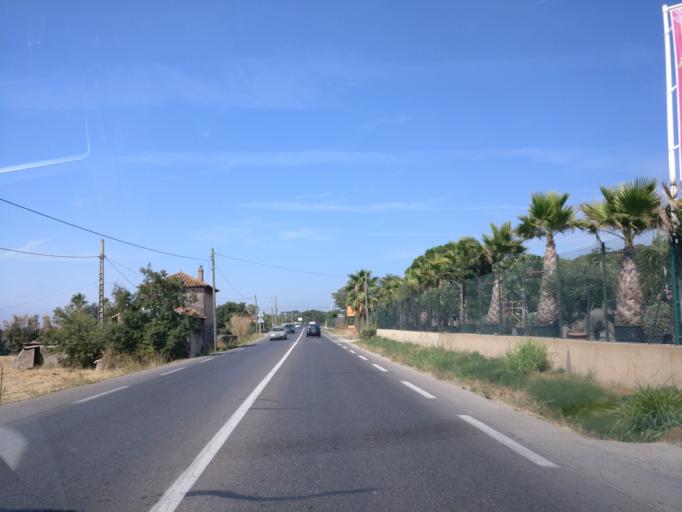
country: FR
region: Provence-Alpes-Cote d'Azur
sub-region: Departement du Var
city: Ollioules
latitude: 43.1258
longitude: 5.8301
